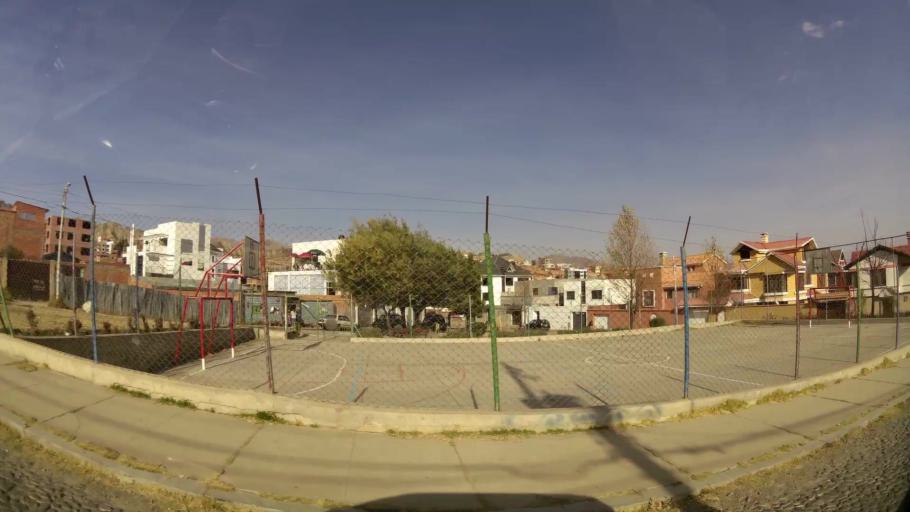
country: BO
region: La Paz
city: La Paz
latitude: -16.5090
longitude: -68.0839
